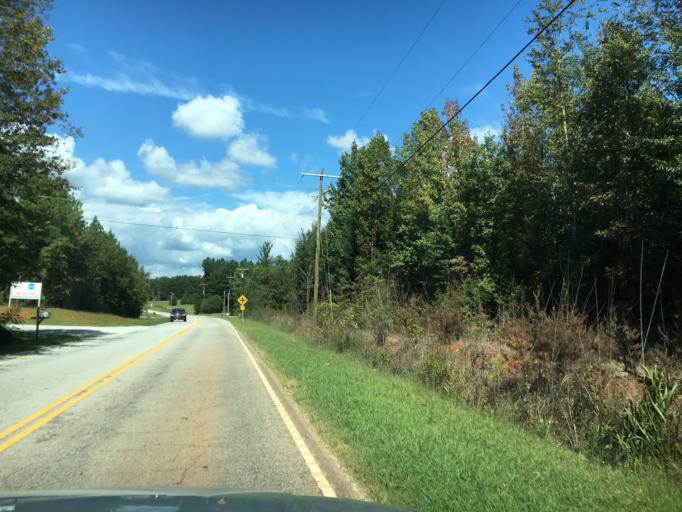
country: US
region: South Carolina
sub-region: Greenville County
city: Tigerville
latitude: 35.0278
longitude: -82.4075
